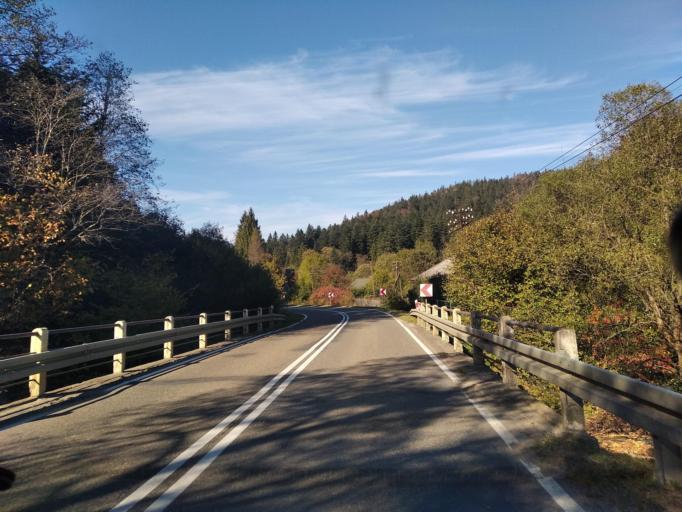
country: PL
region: Subcarpathian Voivodeship
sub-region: Powiat leski
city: Baligrod
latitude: 49.2826
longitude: 22.2790
